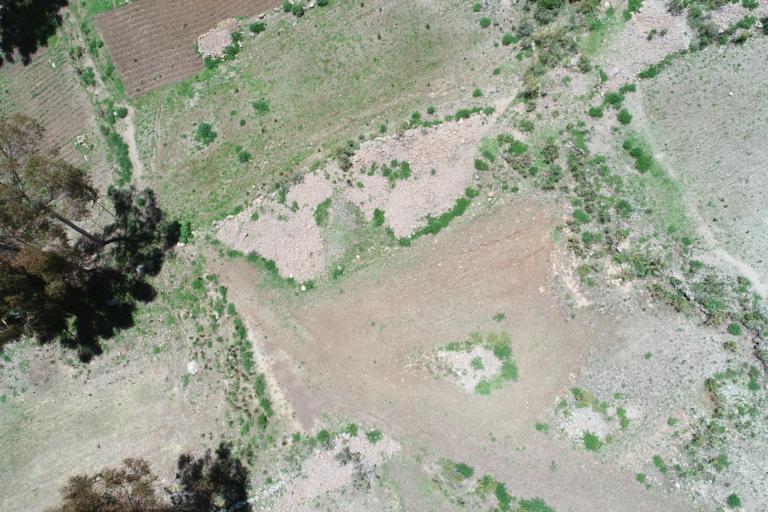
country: BO
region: La Paz
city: Achacachi
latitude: -16.0217
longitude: -68.7936
